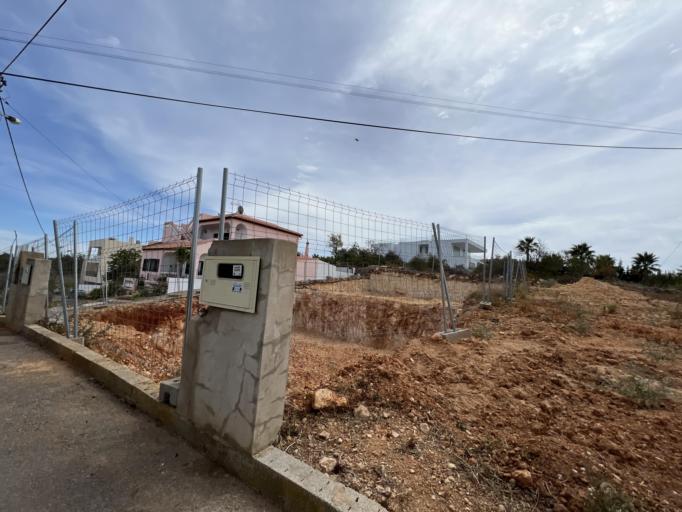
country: PT
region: Faro
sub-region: Portimao
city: Portimao
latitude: 37.1236
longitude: -8.5149
